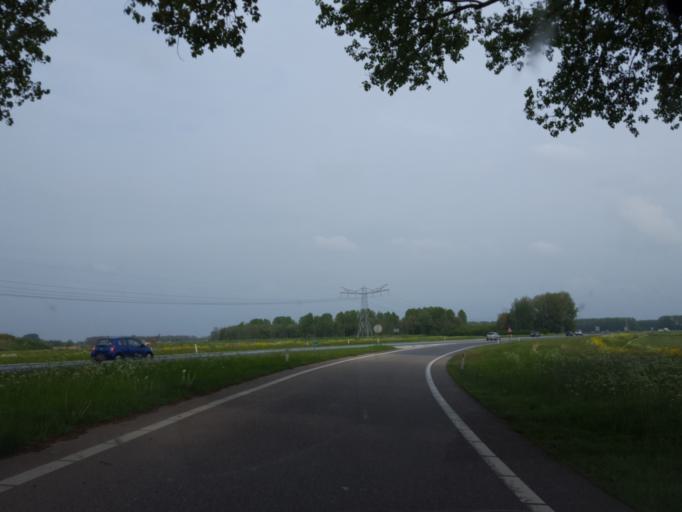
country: NL
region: Gelderland
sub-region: Gemeente Wijchen
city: Bergharen
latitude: 51.8713
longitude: 5.6644
